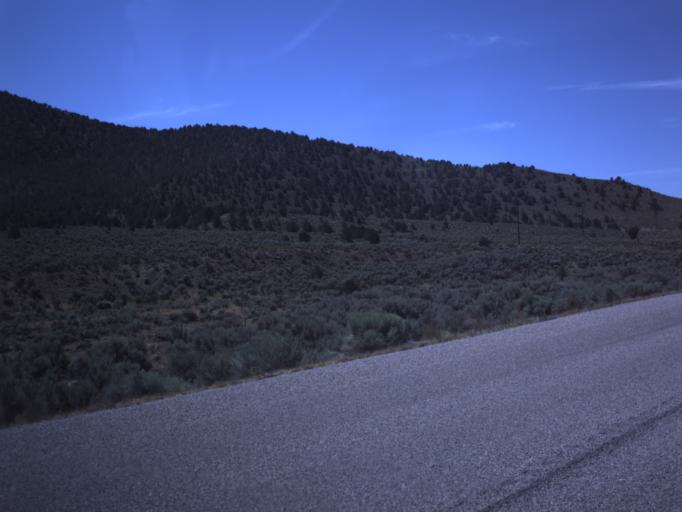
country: US
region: Utah
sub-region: Piute County
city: Junction
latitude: 38.0703
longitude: -112.3433
